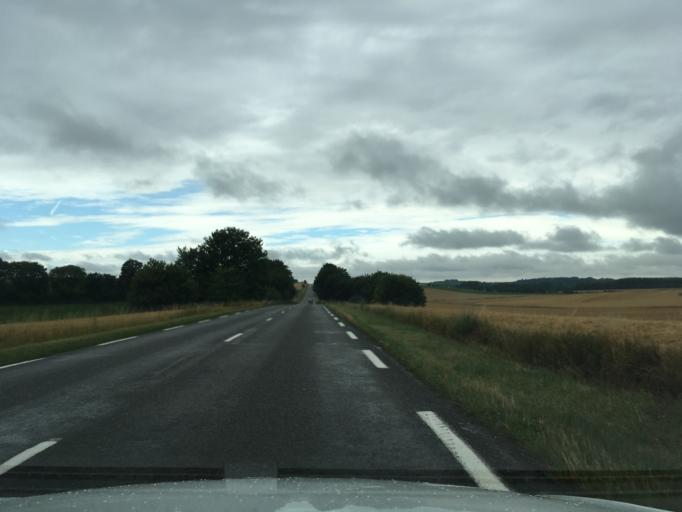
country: FR
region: Picardie
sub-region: Departement de l'Aisne
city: Origny-Sainte-Benoite
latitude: 49.8522
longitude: 3.5229
